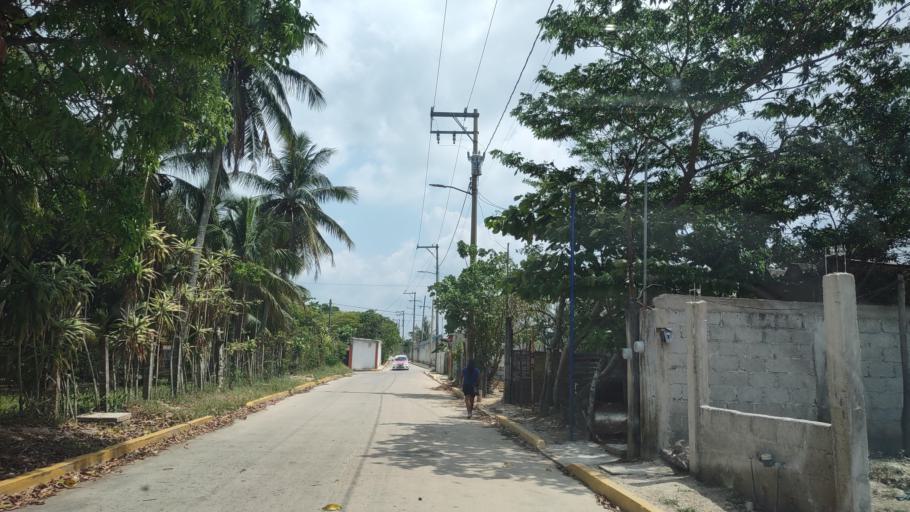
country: MX
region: Veracruz
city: Las Choapas
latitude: 17.9072
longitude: -94.1104
